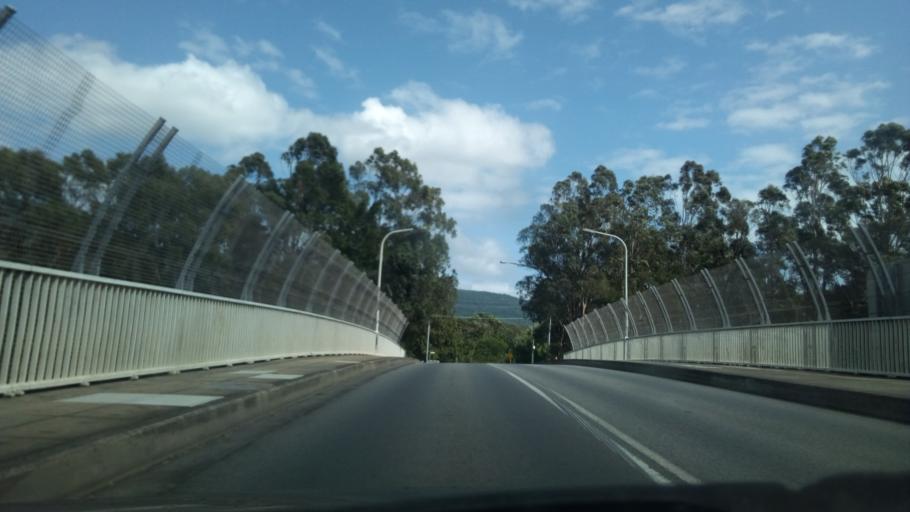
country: AU
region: New South Wales
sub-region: Wollongong
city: Gwynneville
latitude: -34.4115
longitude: 150.8870
